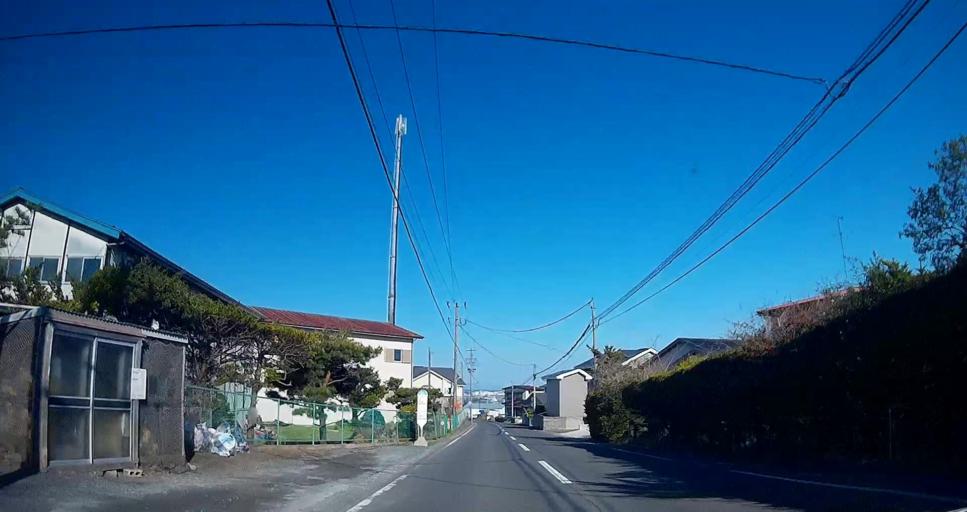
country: JP
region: Aomori
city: Hachinohe
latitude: 40.5228
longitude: 141.5583
